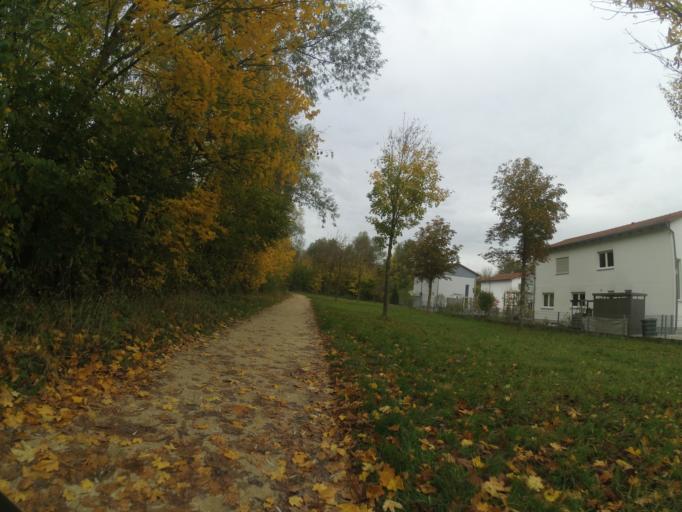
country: DE
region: Bavaria
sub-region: Swabia
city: Neu-Ulm
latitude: 48.3745
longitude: 10.0157
